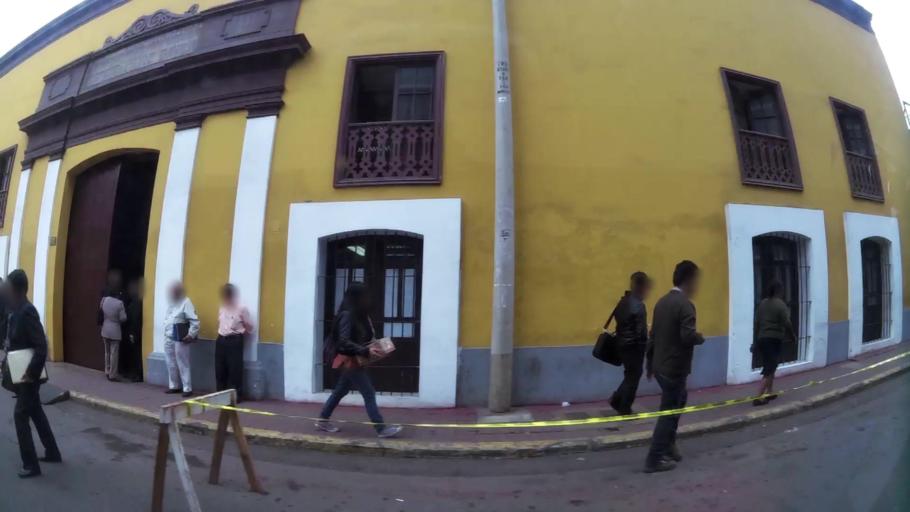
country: PE
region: Lima
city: Lima
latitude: -12.0467
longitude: -77.0255
